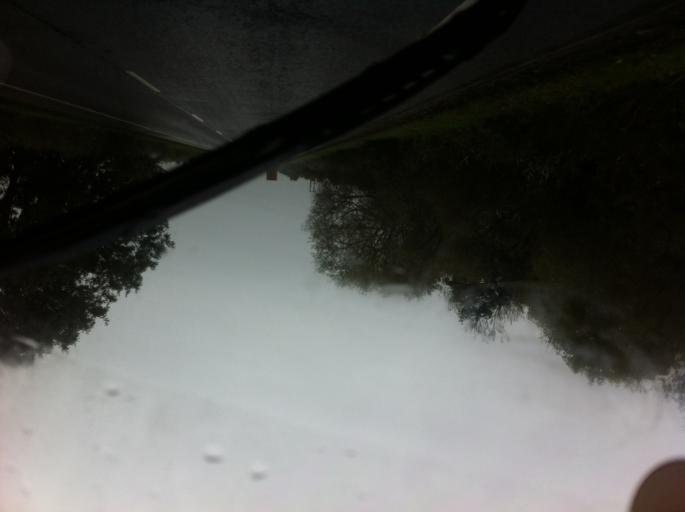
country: GB
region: England
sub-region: Lincolnshire
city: Kirton
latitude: 52.9392
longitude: -0.0442
